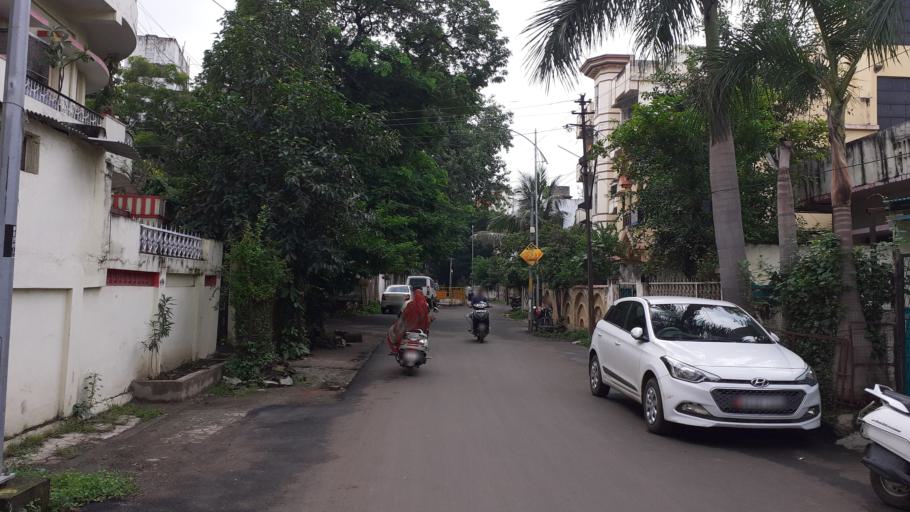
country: IN
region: Maharashtra
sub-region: Nagpur Division
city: Nagpur
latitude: 21.1304
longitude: 79.1137
